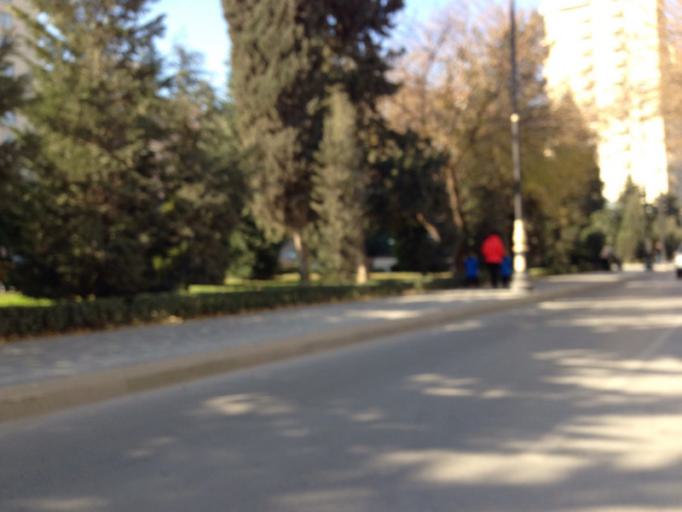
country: AZ
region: Baki
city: Baku
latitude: 40.3991
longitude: 49.8706
